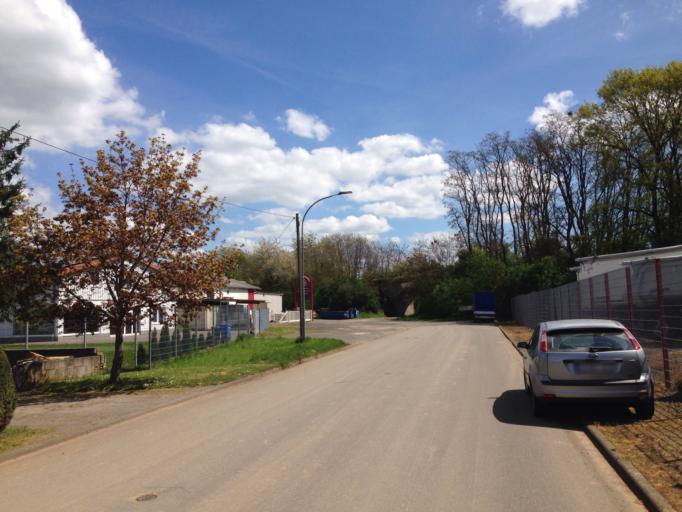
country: DE
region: Hesse
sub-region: Regierungsbezirk Giessen
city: Lich
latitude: 50.5124
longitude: 8.8314
